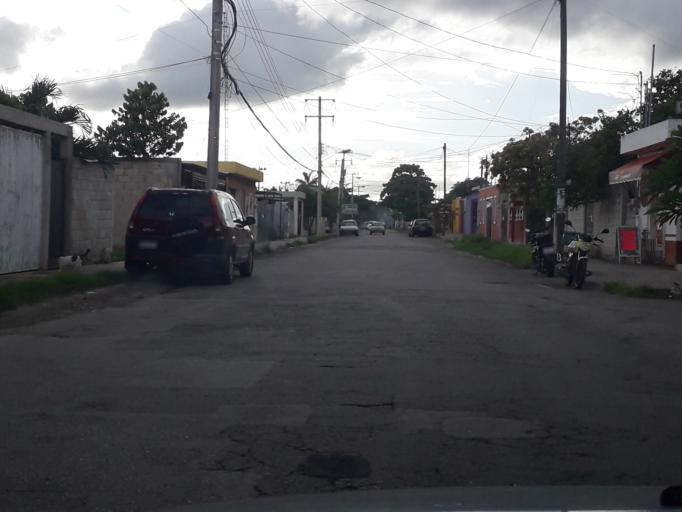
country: MX
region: Yucatan
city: Merida
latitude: 20.9611
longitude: -89.6572
